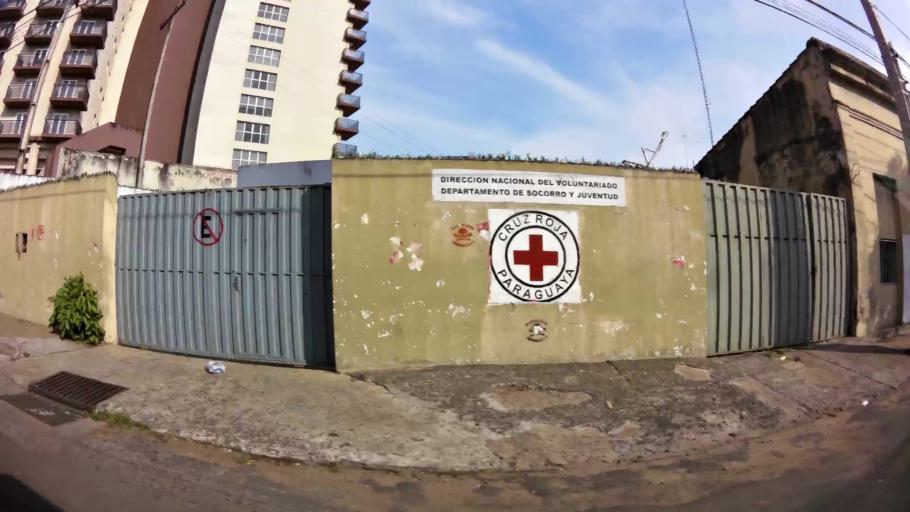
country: PY
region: Asuncion
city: Asuncion
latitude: -25.2845
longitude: -57.6221
